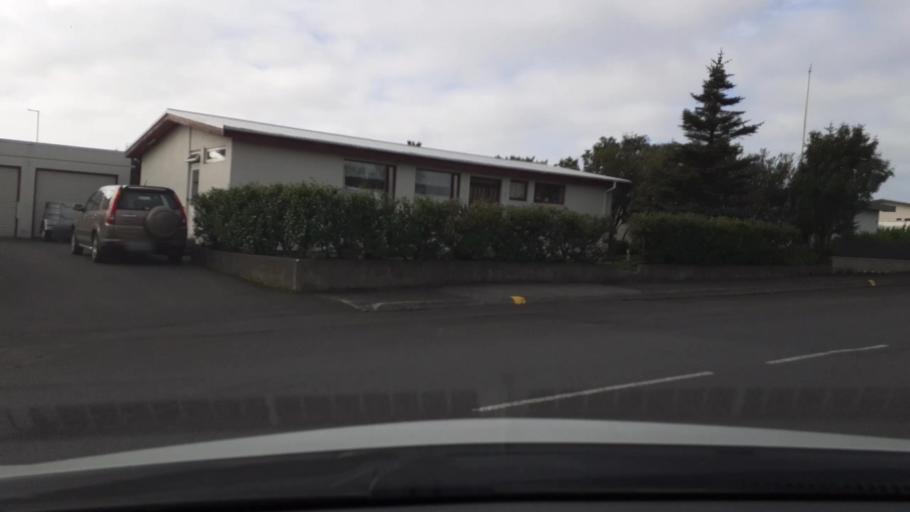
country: IS
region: South
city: THorlakshoefn
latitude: 63.8535
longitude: -21.3894
